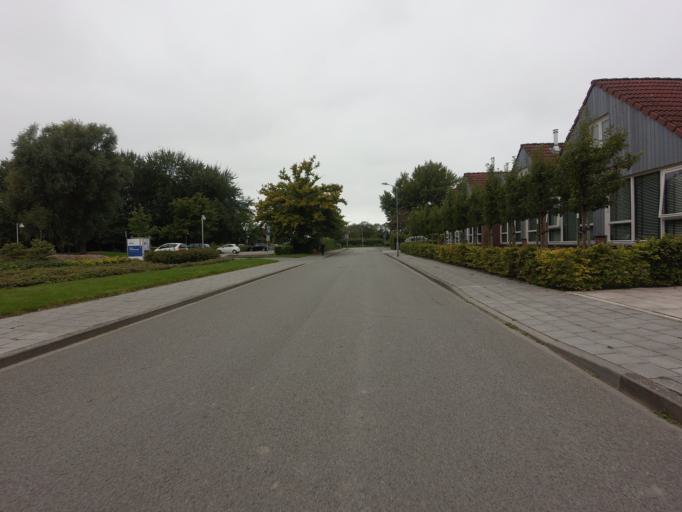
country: NL
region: Zeeland
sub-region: Gemeente Veere
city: Veere
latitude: 51.5423
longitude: 3.6626
